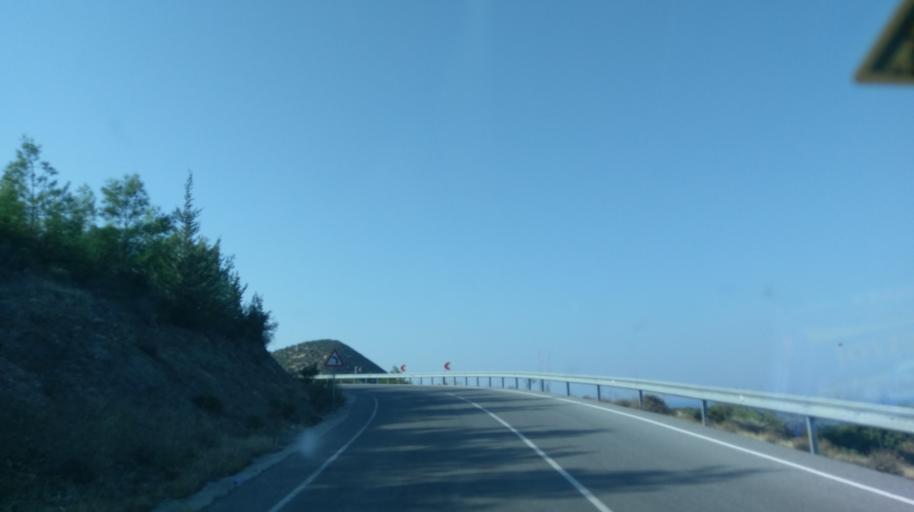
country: CY
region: Lefkosia
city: Kato Pyrgos
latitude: 35.1710
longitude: 32.7239
